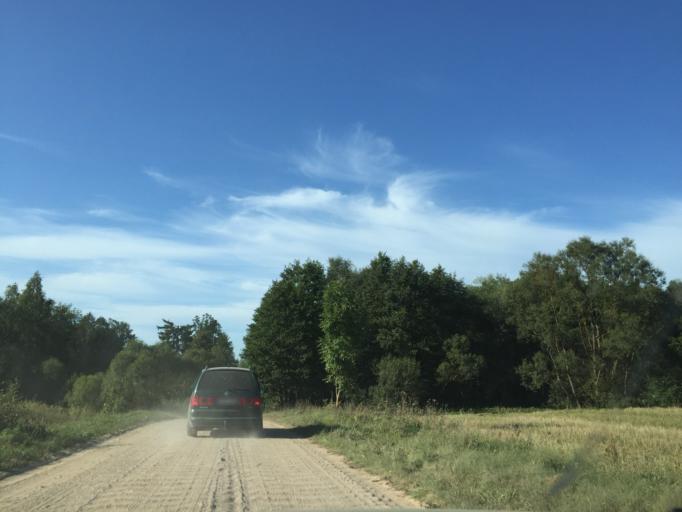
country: LT
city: Zarasai
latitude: 55.7940
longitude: 25.9529
